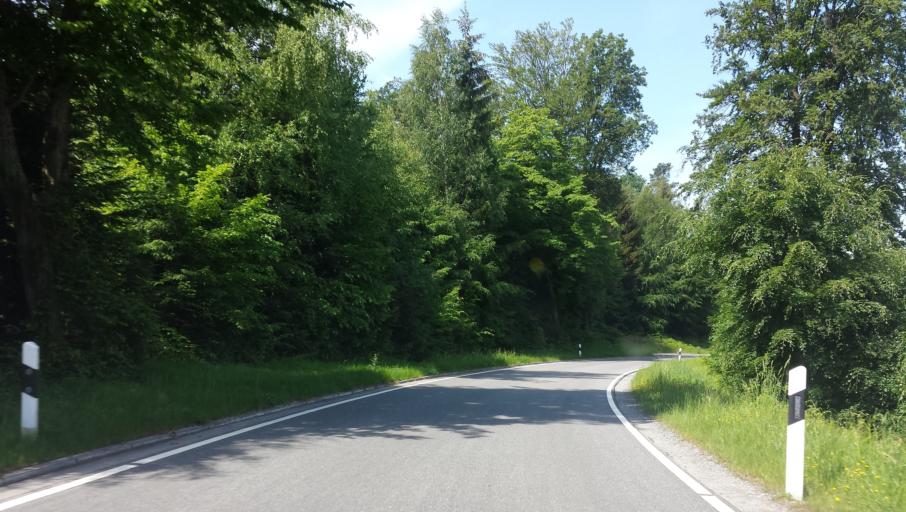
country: DE
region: Hesse
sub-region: Regierungsbezirk Darmstadt
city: Rothenberg
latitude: 49.5188
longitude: 8.9299
